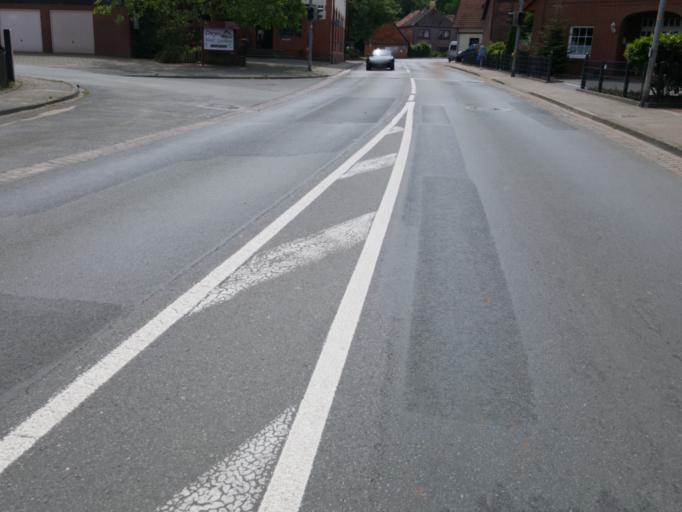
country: DE
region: Lower Saxony
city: Husum
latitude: 52.5661
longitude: 9.2521
